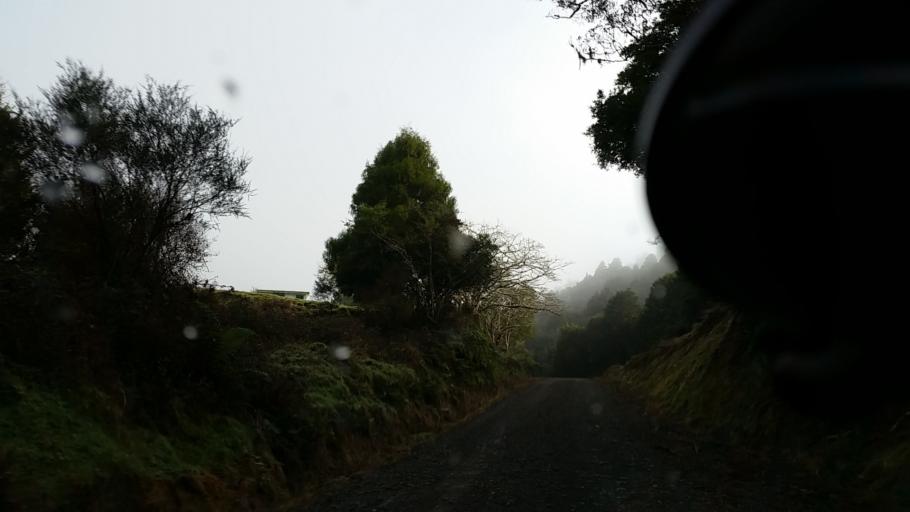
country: NZ
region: Taranaki
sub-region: New Plymouth District
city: Waitara
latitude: -38.9651
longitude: 174.7926
